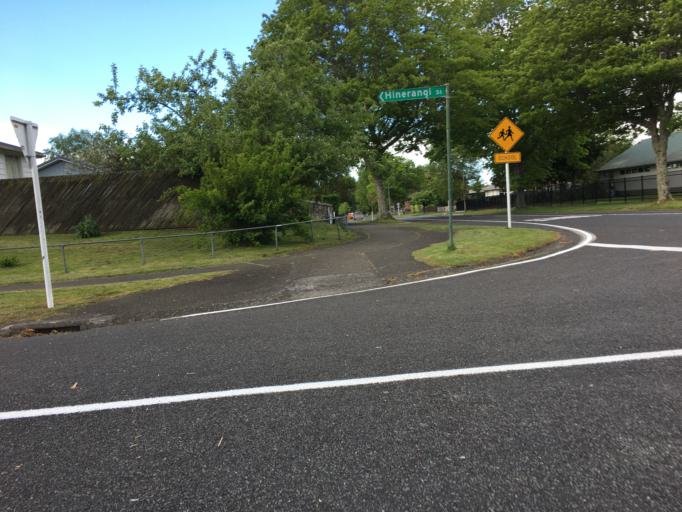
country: NZ
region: Waikato
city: Turangi
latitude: -38.9863
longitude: 175.8118
